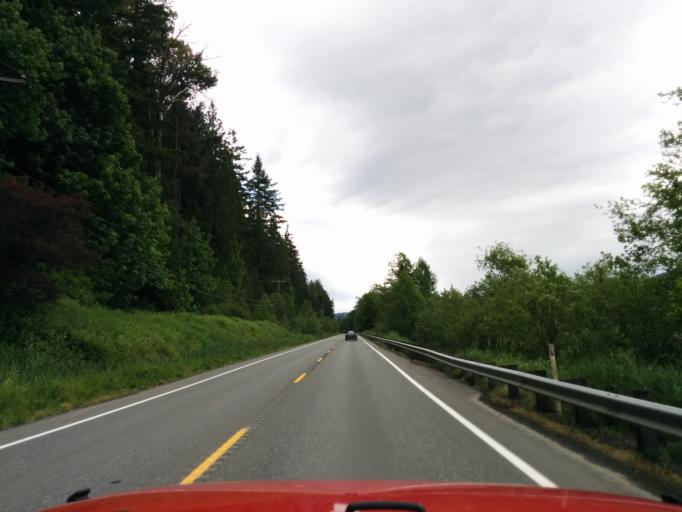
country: US
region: Washington
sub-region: King County
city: Ames Lake
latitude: 47.5843
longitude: -121.9459
